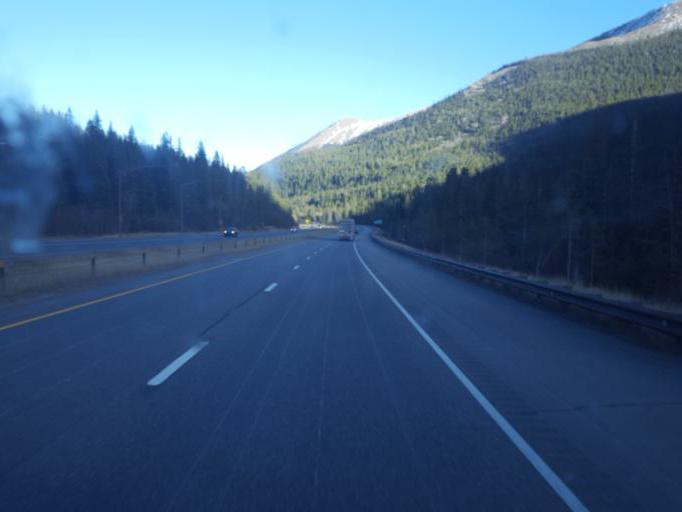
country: US
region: Colorado
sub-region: Clear Creek County
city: Georgetown
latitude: 39.6926
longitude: -105.8161
